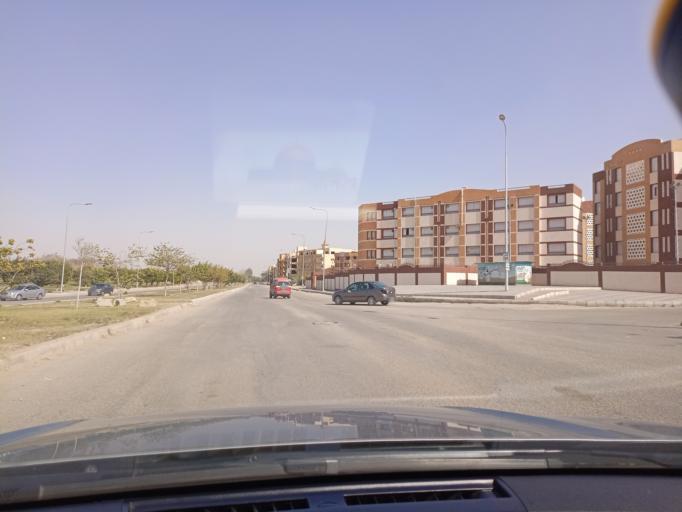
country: EG
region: Muhafazat al Qalyubiyah
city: Al Khankah
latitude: 30.2271
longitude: 31.4480
